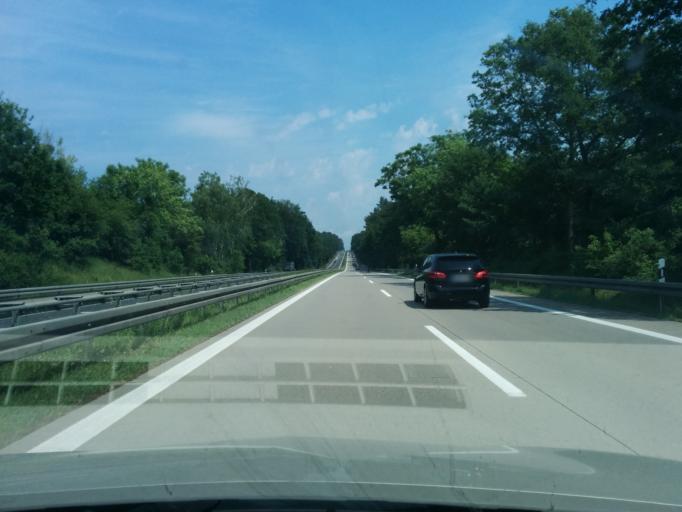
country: DE
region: Brandenburg
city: Britz
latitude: 52.9020
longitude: 13.7359
